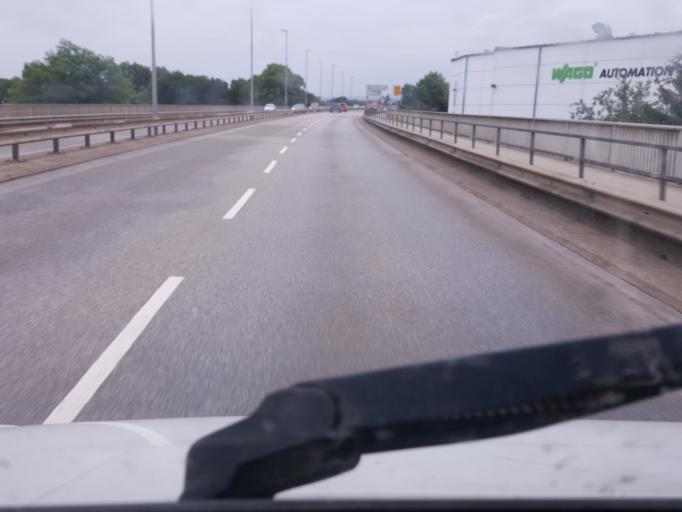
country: DE
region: North Rhine-Westphalia
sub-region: Regierungsbezirk Detmold
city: Minden
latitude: 52.2989
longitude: 8.9232
